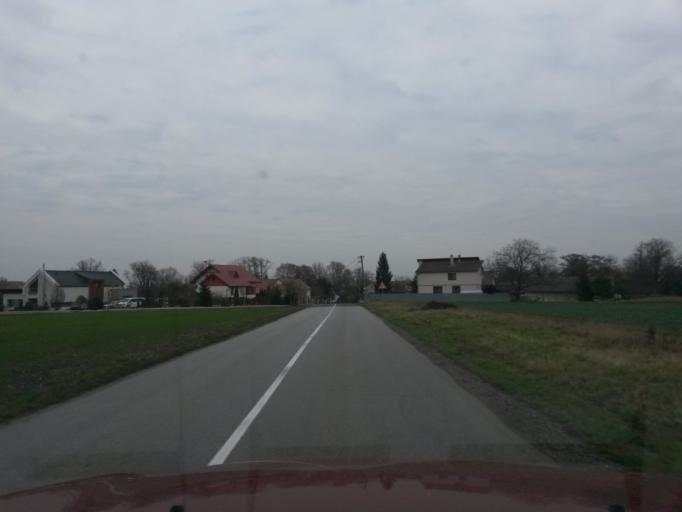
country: SK
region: Kosicky
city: Trebisov
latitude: 48.6332
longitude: 21.6606
